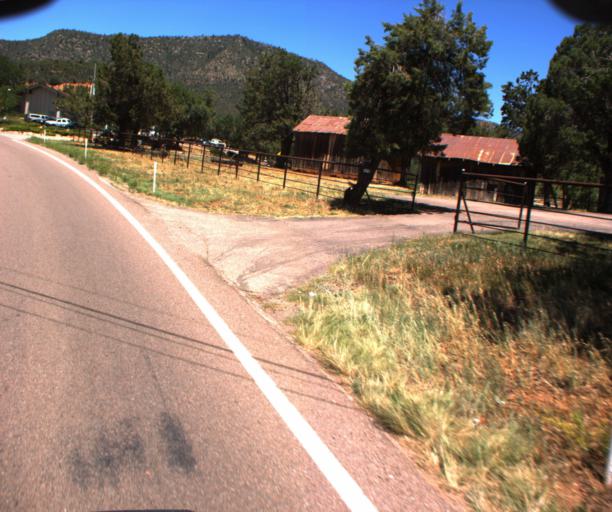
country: US
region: Arizona
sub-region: Gila County
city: Pine
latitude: 34.3910
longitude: -111.4553
